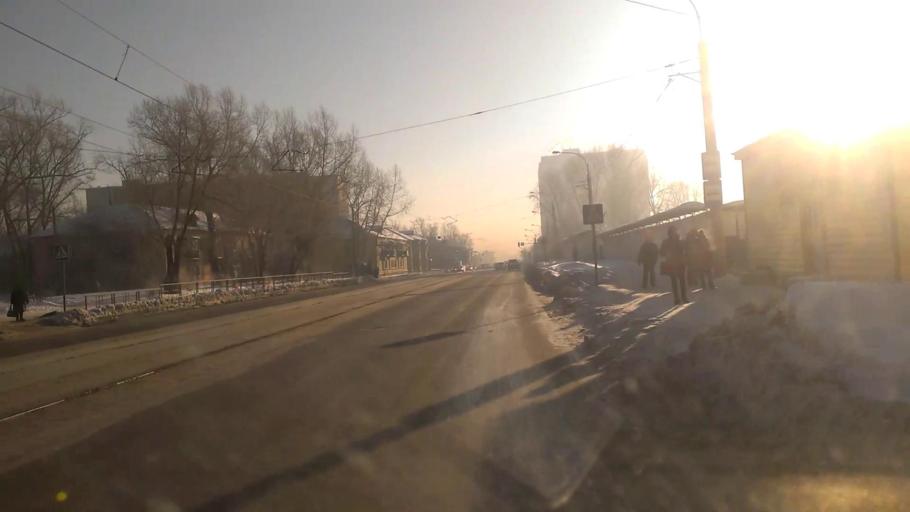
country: RU
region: Altai Krai
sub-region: Gorod Barnaulskiy
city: Barnaul
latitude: 53.3486
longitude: 83.7295
